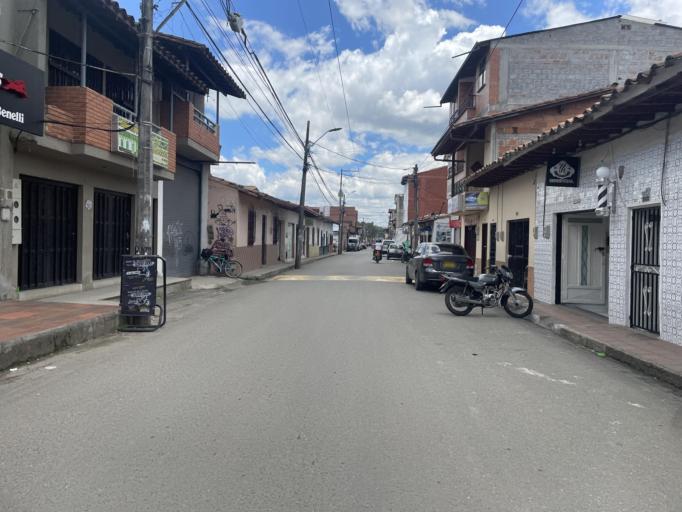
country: CO
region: Antioquia
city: La Ceja
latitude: 6.0336
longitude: -75.4304
